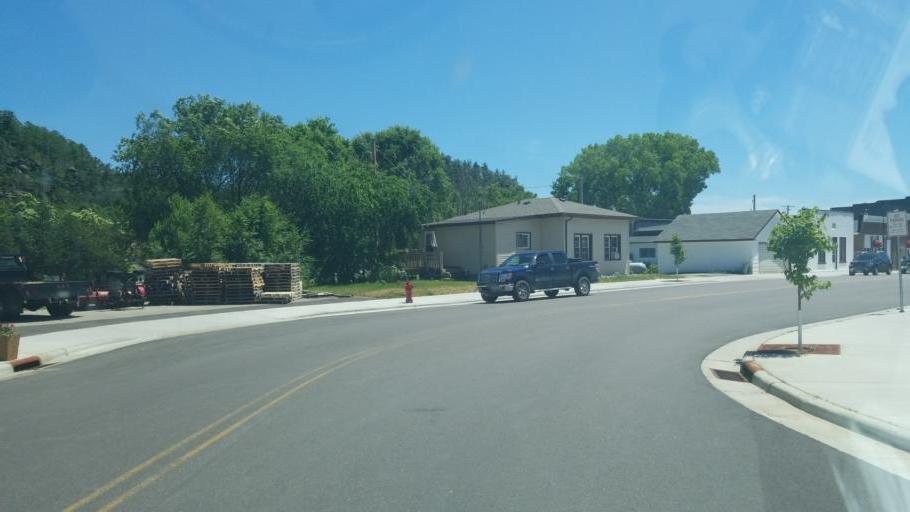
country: US
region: Wisconsin
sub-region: Juneau County
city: New Lisbon
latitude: 43.9204
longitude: -90.2689
